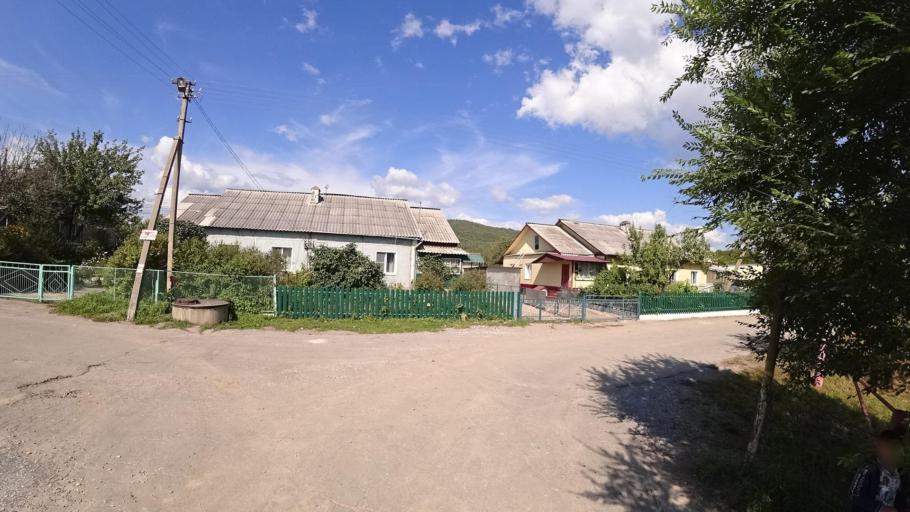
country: RU
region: Jewish Autonomous Oblast
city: Londoko
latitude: 49.0173
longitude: 131.8871
